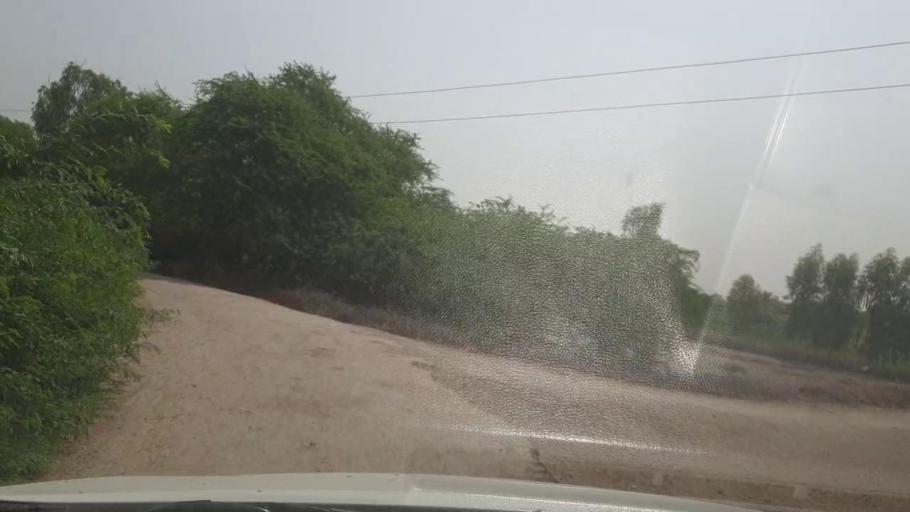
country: PK
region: Sindh
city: Kot Diji
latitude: 27.3429
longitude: 68.7150
